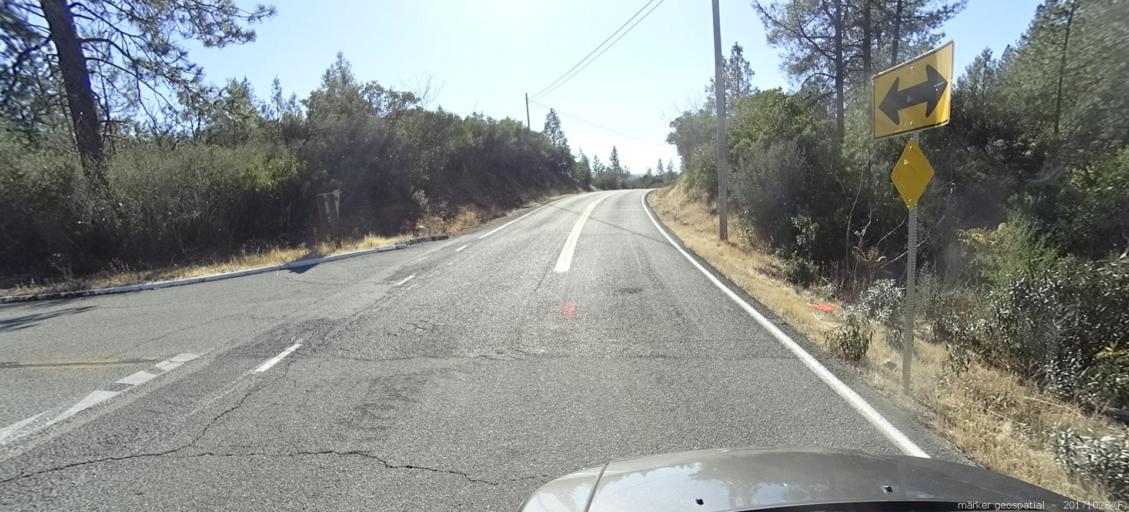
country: US
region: California
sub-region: Shasta County
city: Shasta
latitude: 40.6342
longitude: -122.4574
